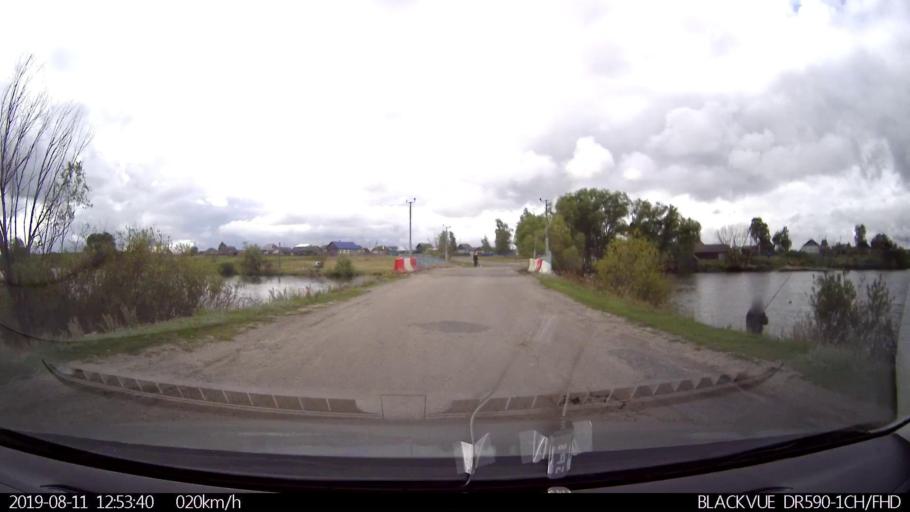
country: RU
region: Ulyanovsk
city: Ignatovka
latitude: 53.8749
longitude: 47.6504
